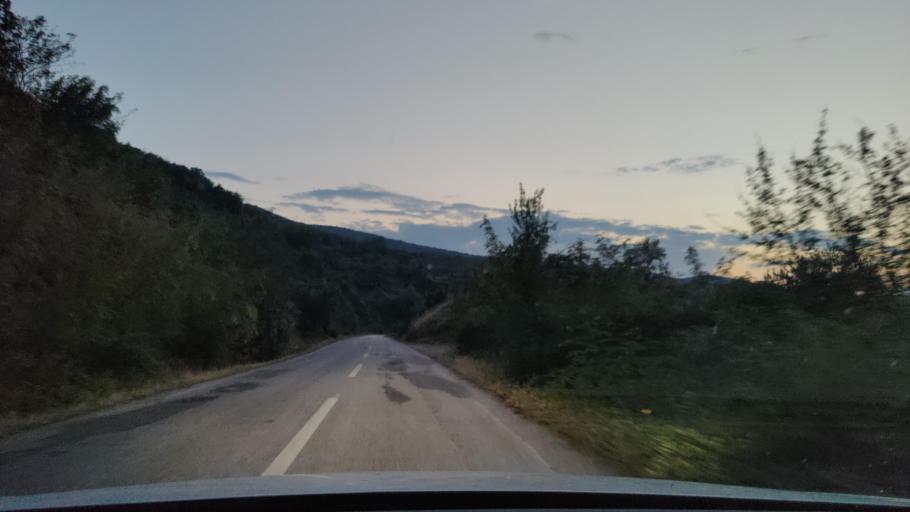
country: GR
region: Central Macedonia
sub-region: Nomos Serron
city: Chrysochorafa
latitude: 41.1974
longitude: 23.0865
